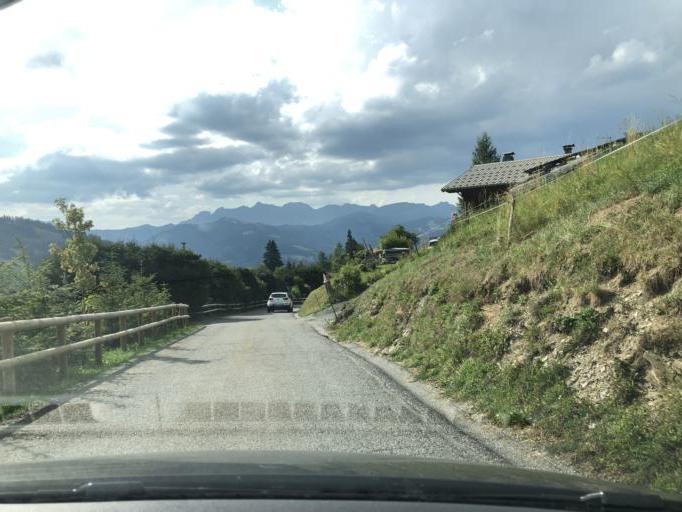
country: FR
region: Rhone-Alpes
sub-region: Departement de la Haute-Savoie
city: Megeve
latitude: 45.8364
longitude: 6.6480
